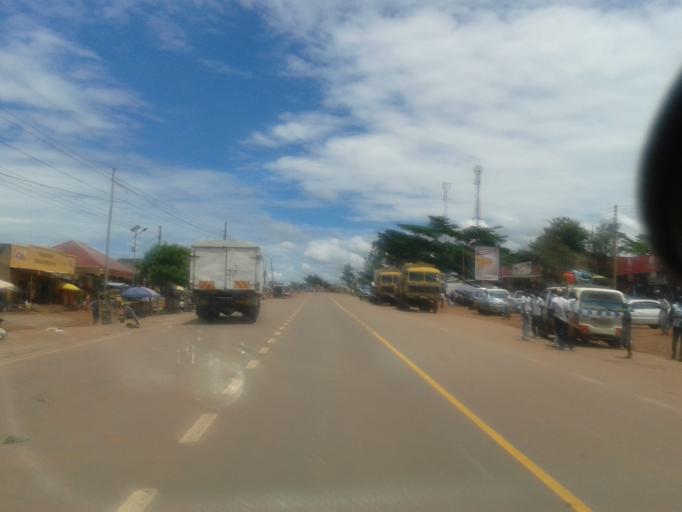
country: UG
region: Western Region
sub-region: Kiryandongo District
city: Kiryandongo
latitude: 1.8093
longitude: 32.0115
